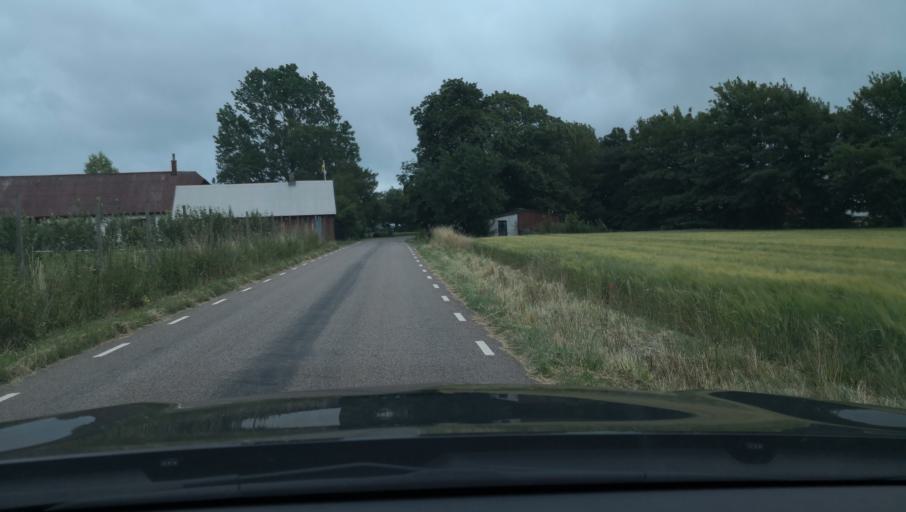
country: SE
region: Skane
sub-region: Simrishamns Kommun
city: Kivik
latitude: 55.6708
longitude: 14.2021
